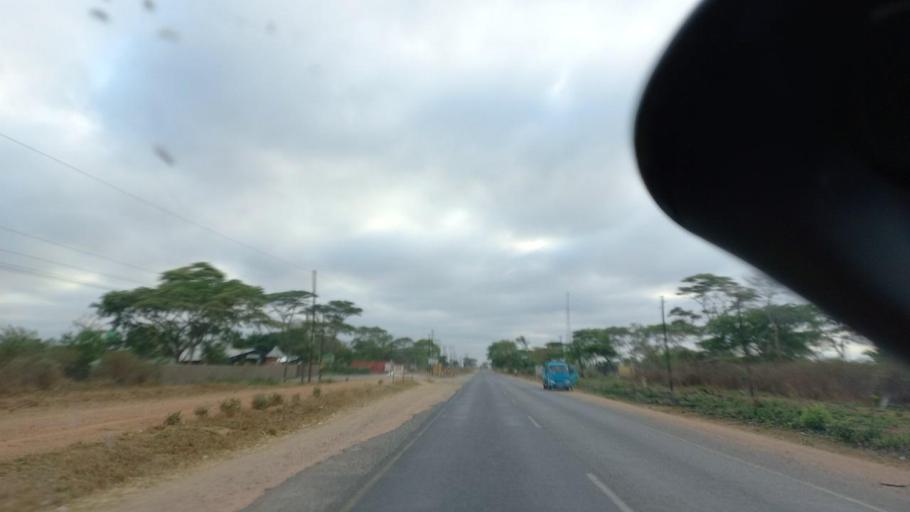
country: ZM
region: Lusaka
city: Chongwe
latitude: -15.3453
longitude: 28.5099
